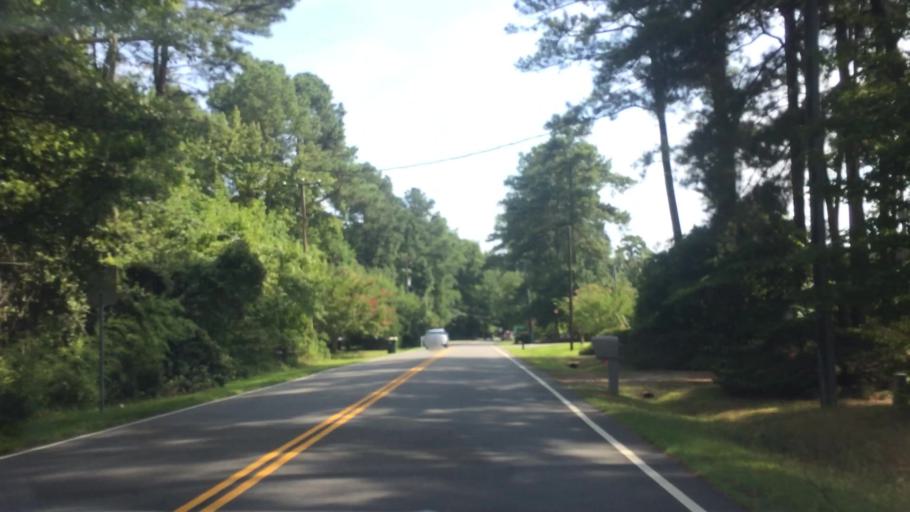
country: US
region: Virginia
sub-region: York County
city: Yorktown
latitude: 37.1661
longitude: -76.4519
